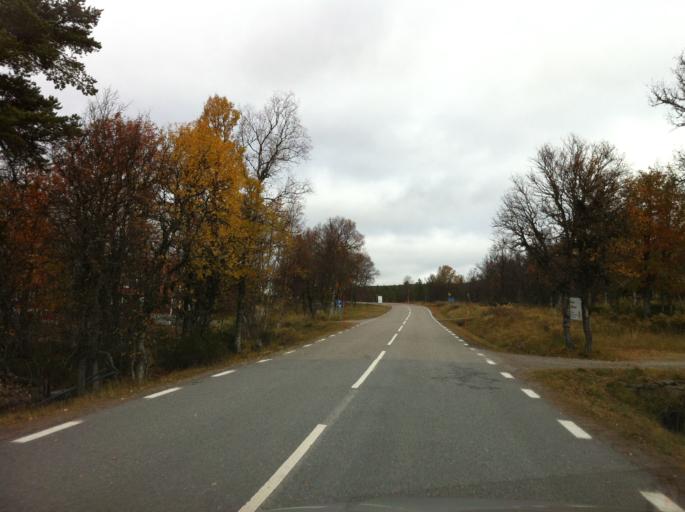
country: NO
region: Hedmark
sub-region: Engerdal
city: Engerdal
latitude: 62.0942
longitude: 12.3106
